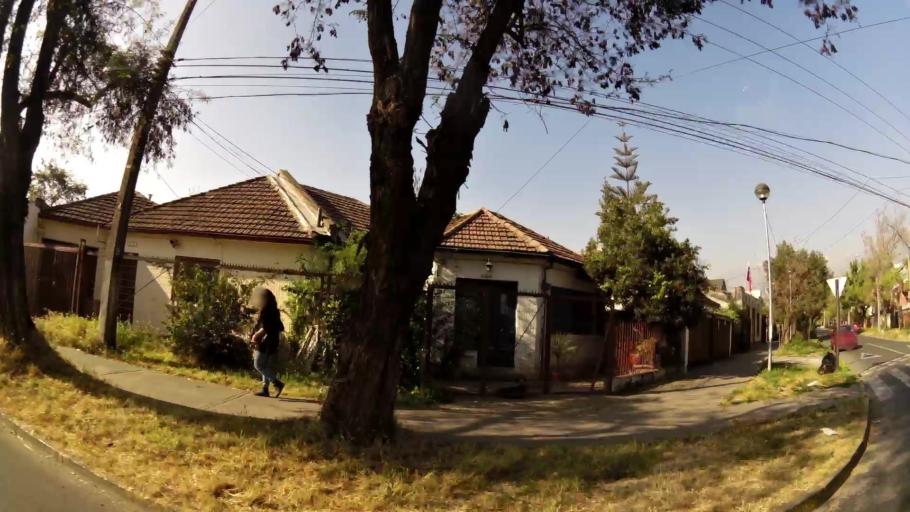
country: CL
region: Santiago Metropolitan
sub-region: Provincia de Santiago
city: Villa Presidente Frei, Nunoa, Santiago, Chile
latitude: -33.4532
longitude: -70.5823
